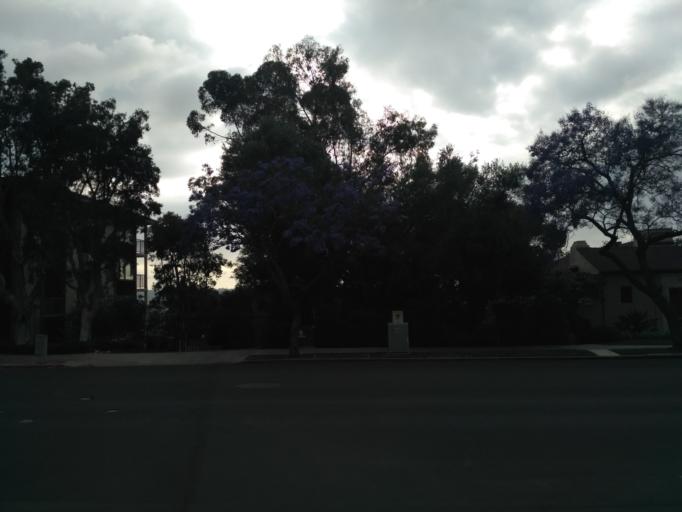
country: US
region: California
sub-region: San Diego County
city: San Diego
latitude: 32.7366
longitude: -117.1638
